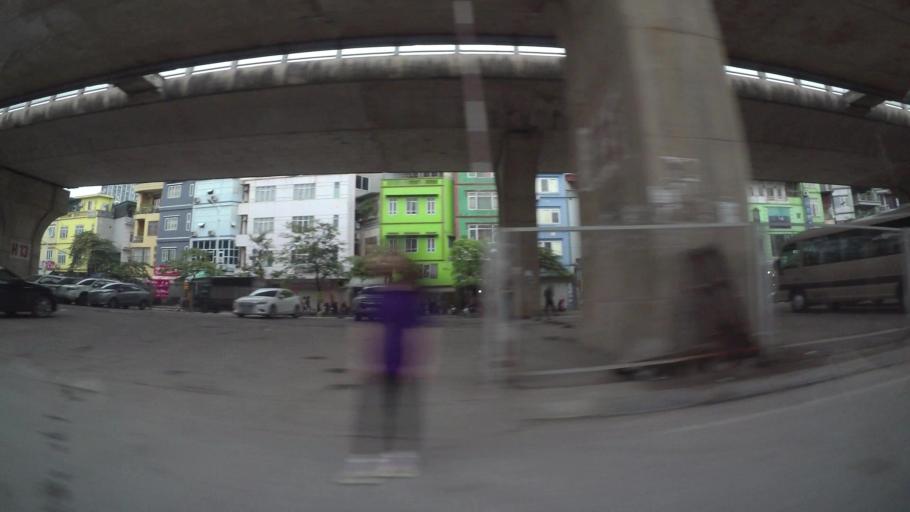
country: VN
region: Ha Noi
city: Hai BaTrung
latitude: 21.0015
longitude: 105.8730
